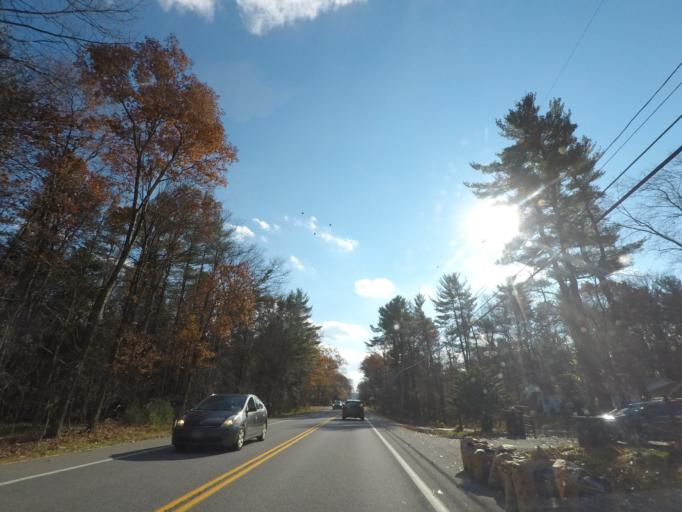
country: US
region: New York
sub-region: Schenectady County
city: East Glenville
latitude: 42.8714
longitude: -73.8877
